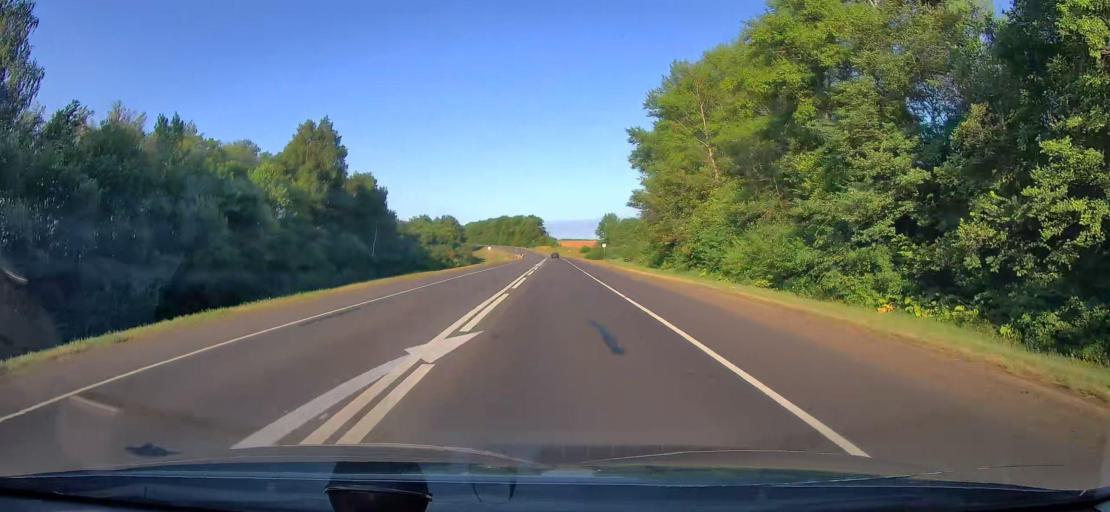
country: RU
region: Tula
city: Plavsk
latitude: 53.6795
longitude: 37.2524
